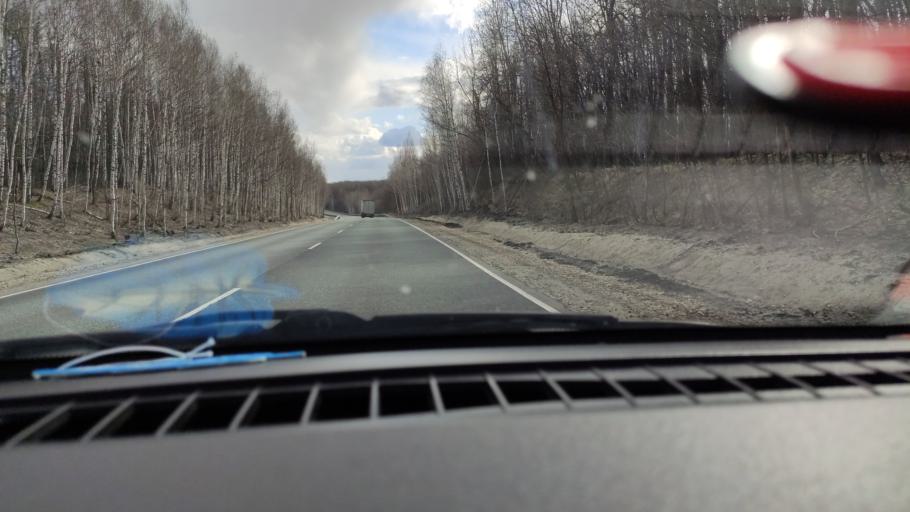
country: RU
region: Saratov
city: Khvalynsk
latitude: 52.4423
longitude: 48.0096
